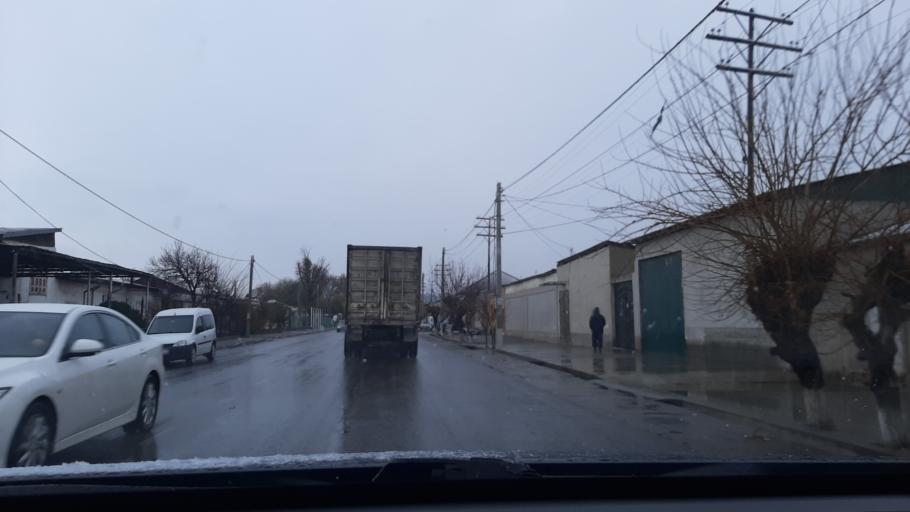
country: TJ
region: Viloyati Sughd
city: Khujand
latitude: 40.2690
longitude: 69.6278
